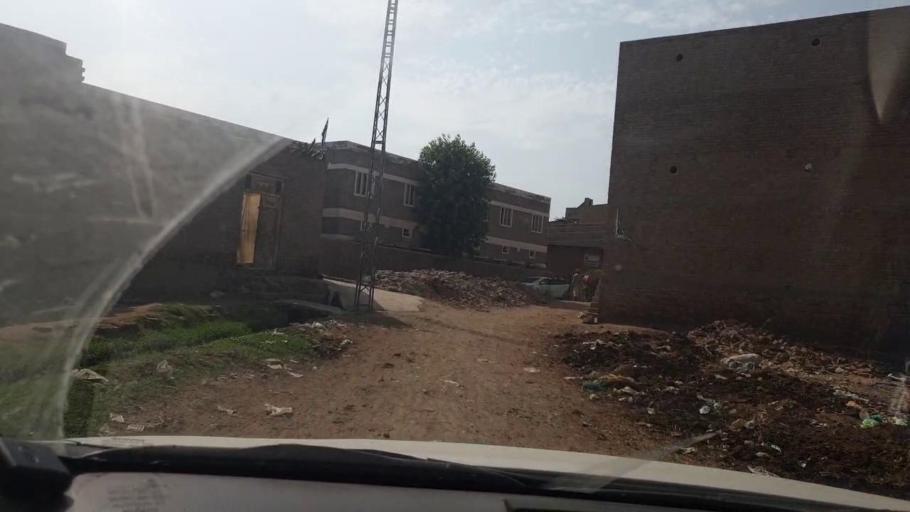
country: PK
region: Sindh
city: Chak
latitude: 27.8305
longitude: 68.7754
